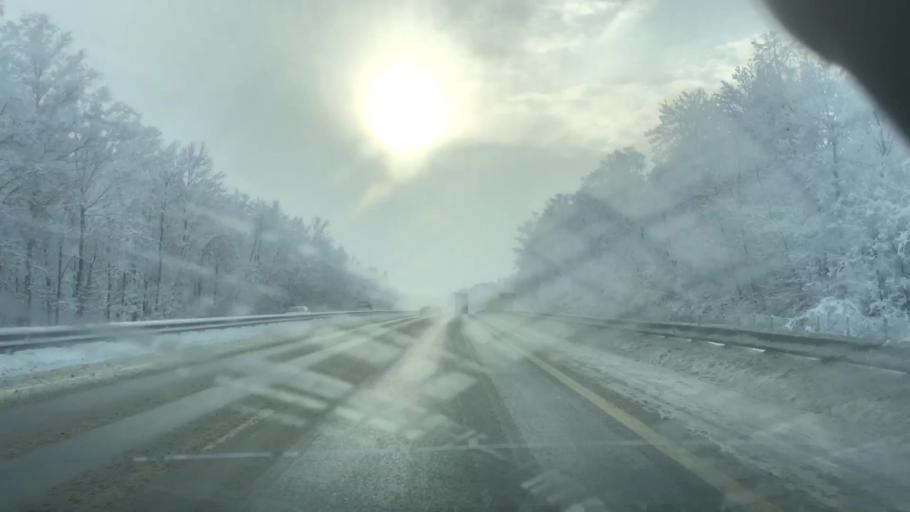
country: RU
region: Tula
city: Venev
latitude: 54.5240
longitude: 38.1683
